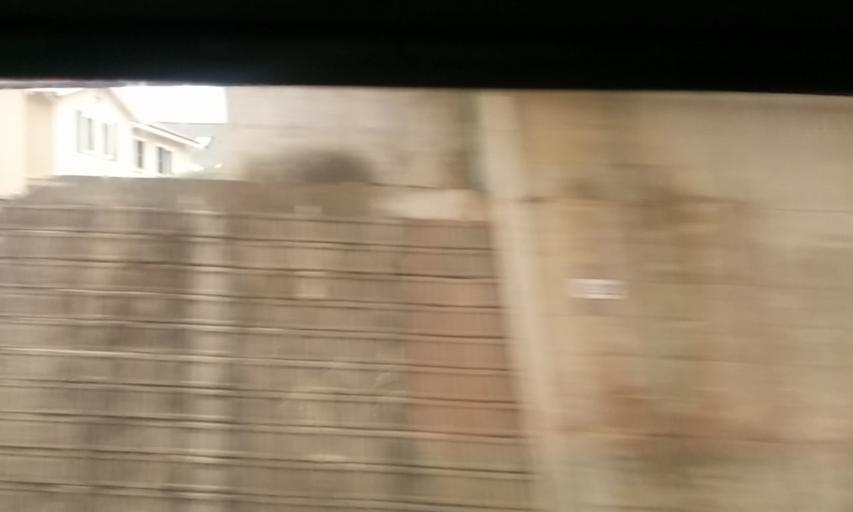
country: JP
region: Nagano
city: Shiojiri
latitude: 36.1295
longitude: 137.9487
